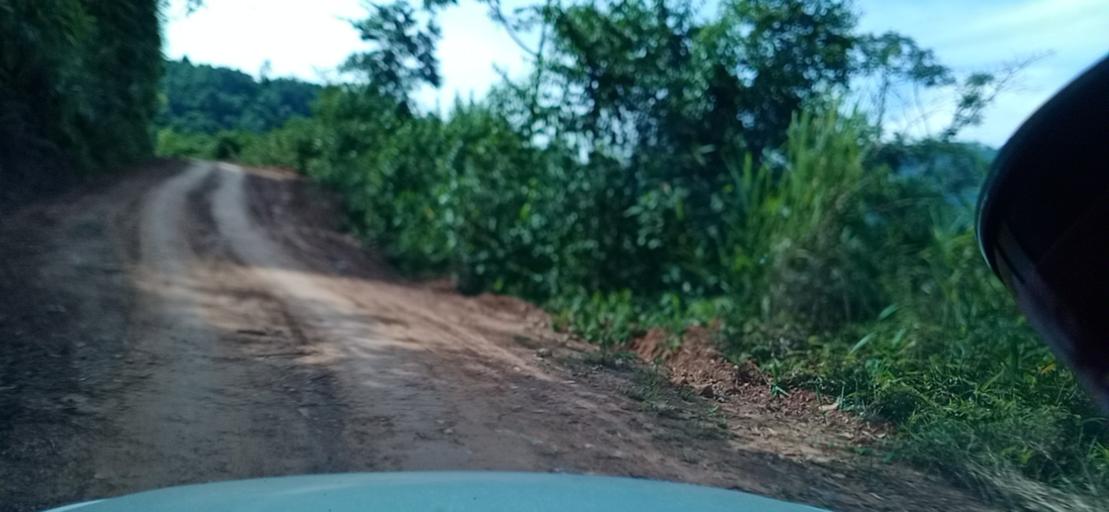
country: TH
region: Changwat Bueng Kan
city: Pak Khat
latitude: 18.6358
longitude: 103.2601
